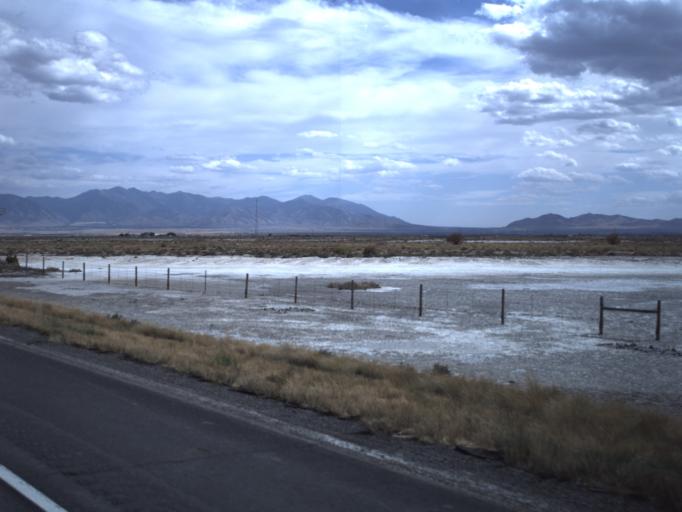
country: US
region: Utah
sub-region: Tooele County
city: Grantsville
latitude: 40.6926
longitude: -112.4677
